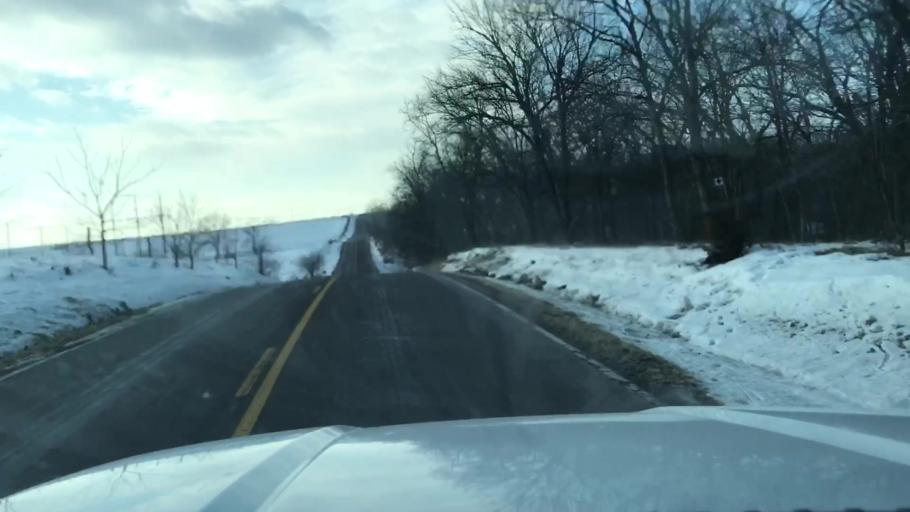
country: US
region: Missouri
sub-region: Nodaway County
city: Maryville
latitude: 40.2020
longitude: -94.9463
